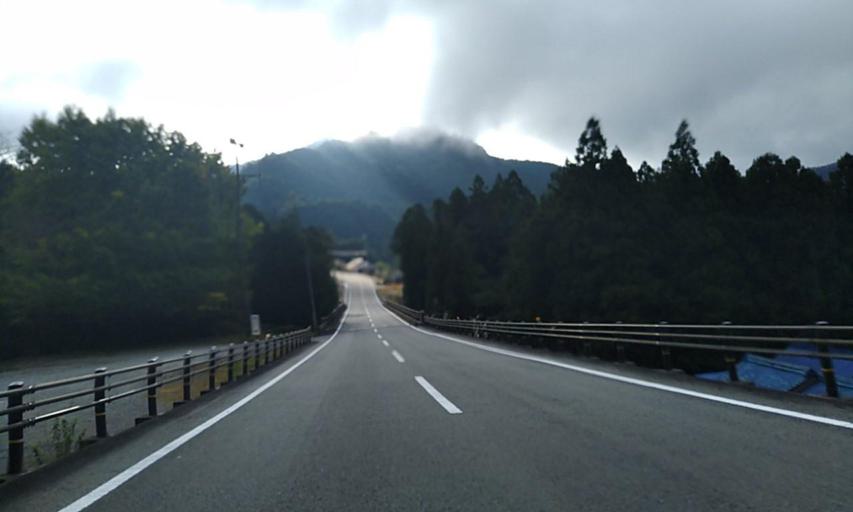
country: JP
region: Wakayama
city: Shingu
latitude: 33.8775
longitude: 135.8643
